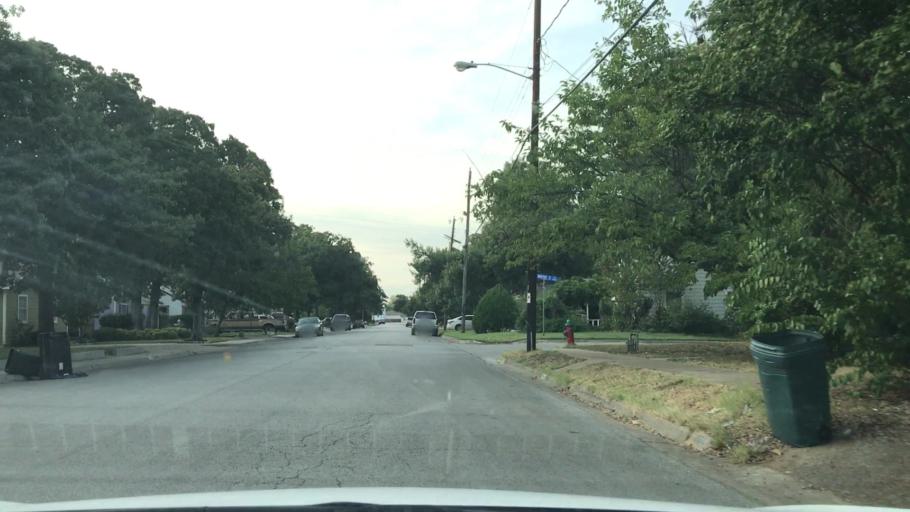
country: US
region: Texas
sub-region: Tarrant County
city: Haltom City
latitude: 32.7917
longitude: -97.2823
